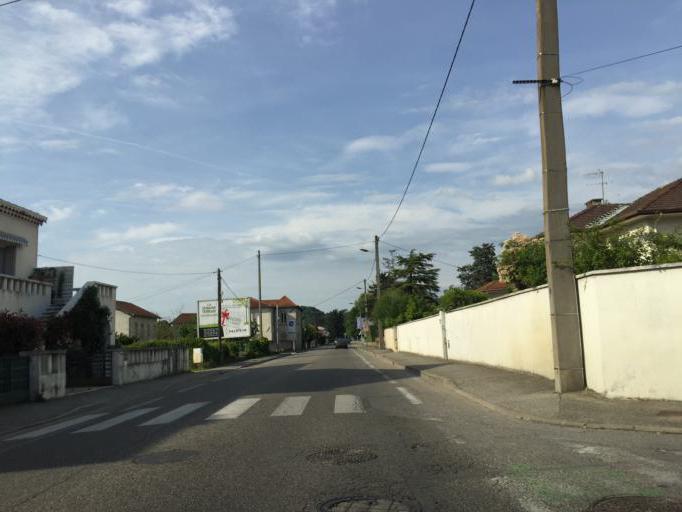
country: FR
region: Rhone-Alpes
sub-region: Departement de la Drome
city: Mours-Saint-Eusebe
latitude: 45.0591
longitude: 5.0503
